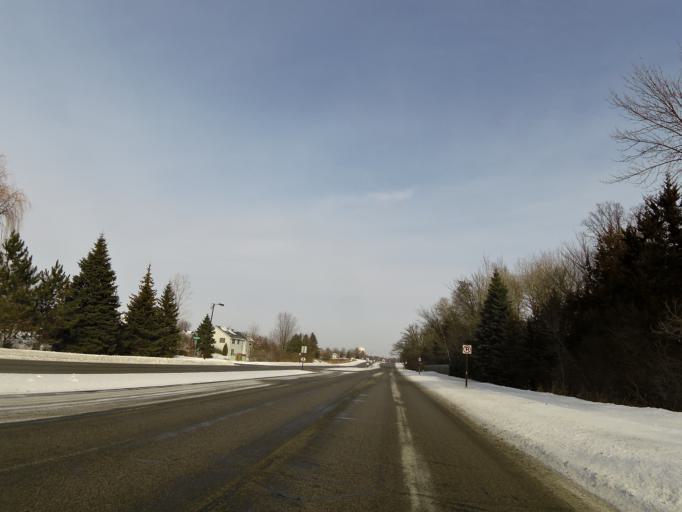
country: US
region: Minnesota
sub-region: Carver County
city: Chanhassen
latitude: 44.8565
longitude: -93.5113
